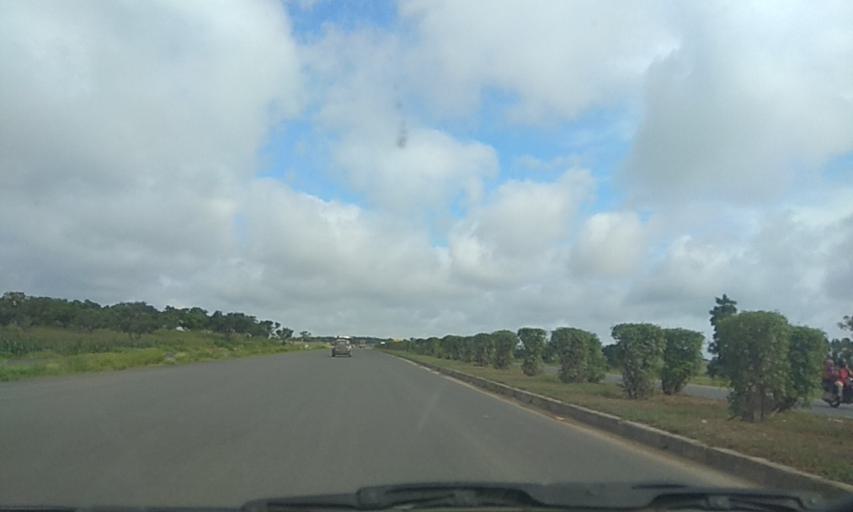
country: IN
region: Karnataka
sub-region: Haveri
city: Shiggaon
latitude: 14.9999
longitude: 75.2079
